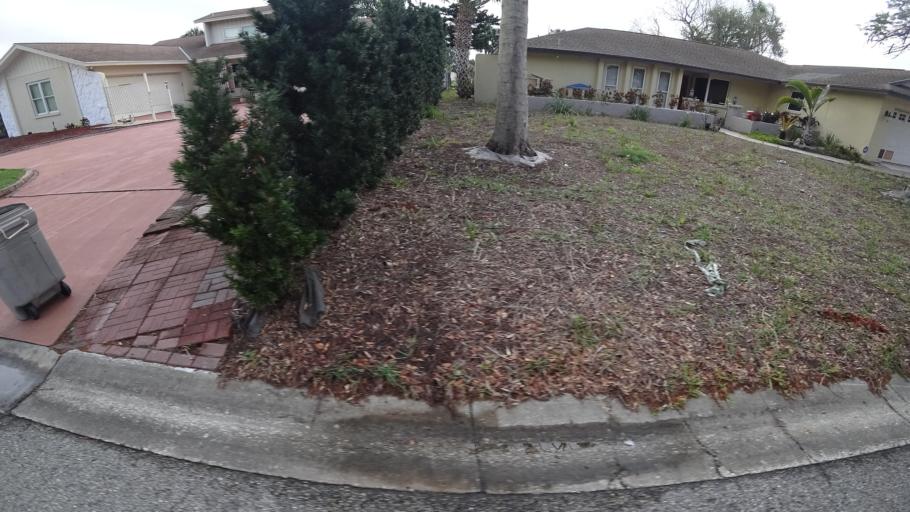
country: US
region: Florida
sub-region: Manatee County
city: Bayshore Gardens
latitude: 27.4303
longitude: -82.6064
